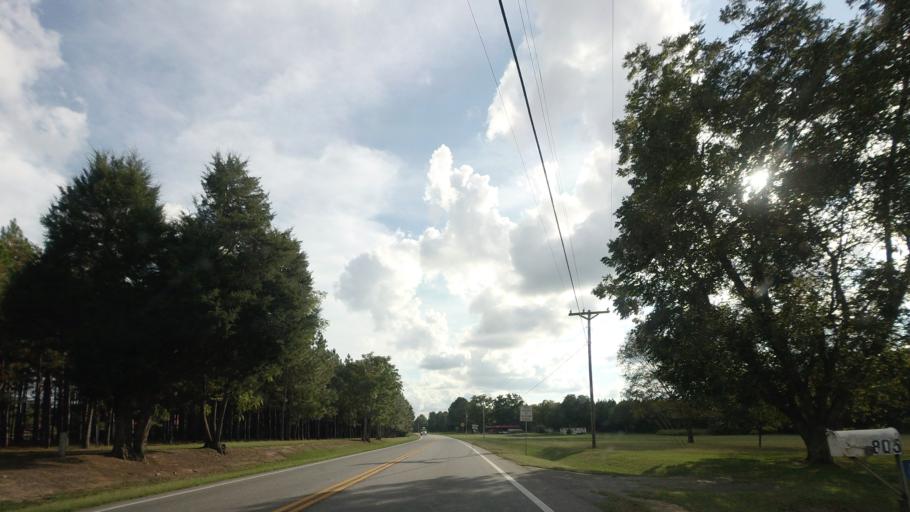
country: US
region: Georgia
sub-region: Pulaski County
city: Hawkinsville
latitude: 32.3276
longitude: -83.4139
